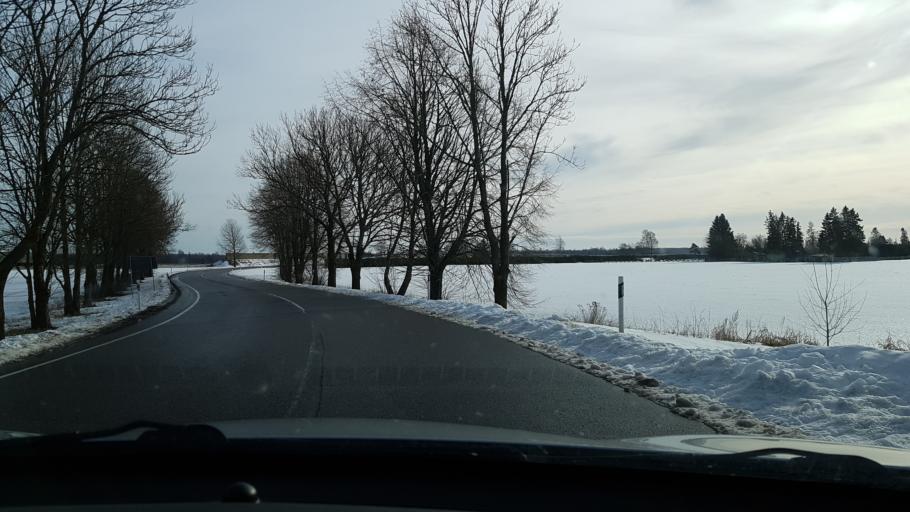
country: EE
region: Jaervamaa
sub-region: Paide linn
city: Paide
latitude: 58.9300
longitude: 25.6075
